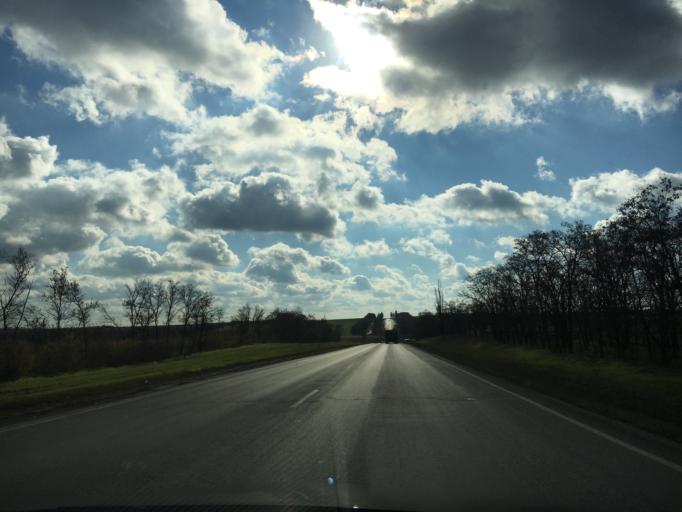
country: RU
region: Rostov
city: Matveyev Kurgan
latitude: 47.5537
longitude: 38.8902
